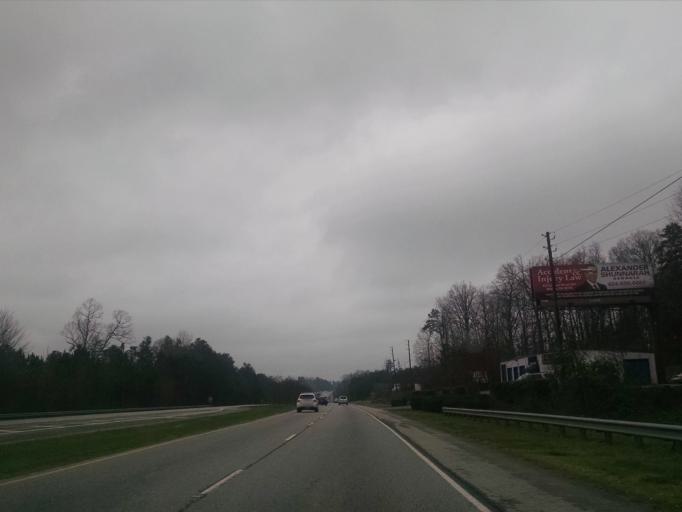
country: US
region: Georgia
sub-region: Gwinnett County
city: Sugar Hill
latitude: 34.0989
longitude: -84.0367
